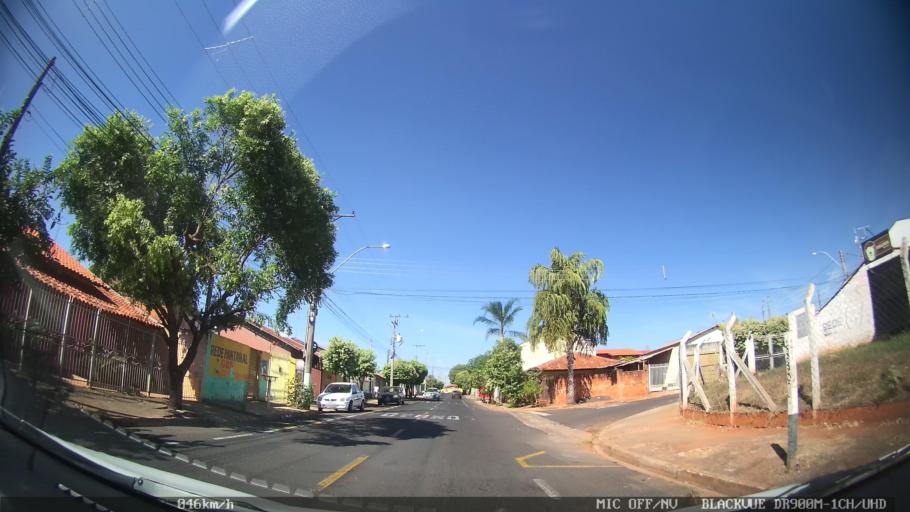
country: BR
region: Sao Paulo
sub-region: Sao Jose Do Rio Preto
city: Sao Jose do Rio Preto
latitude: -20.7649
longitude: -49.4002
